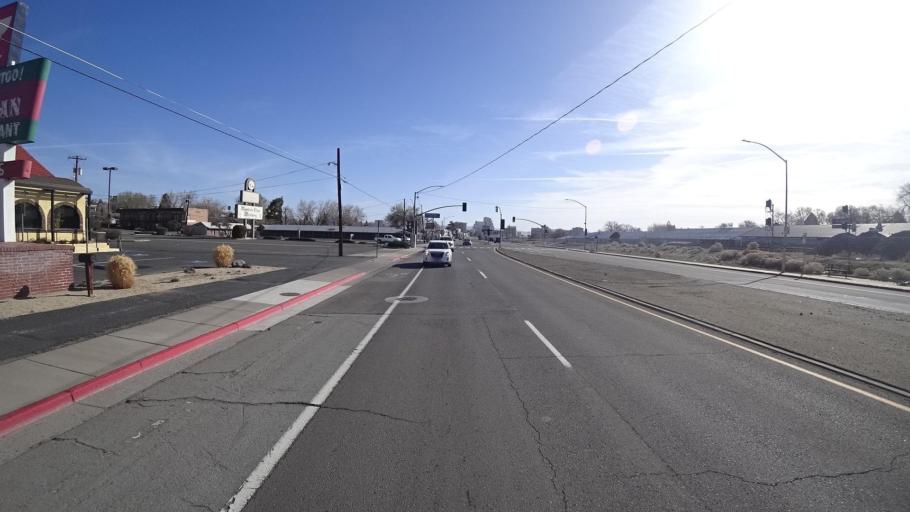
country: US
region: Nevada
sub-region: Washoe County
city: Reno
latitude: 39.5229
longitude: -119.8389
